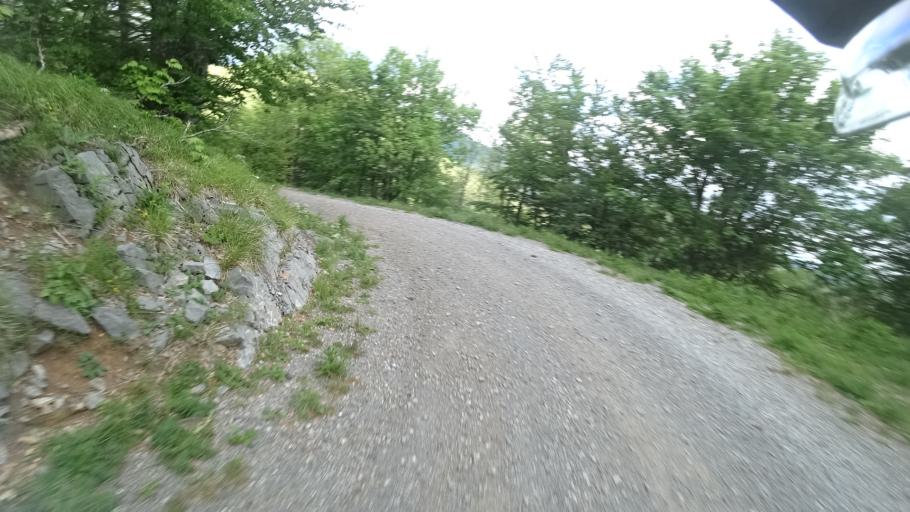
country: HR
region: Licko-Senjska
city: Gospic
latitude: 44.4561
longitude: 15.3001
